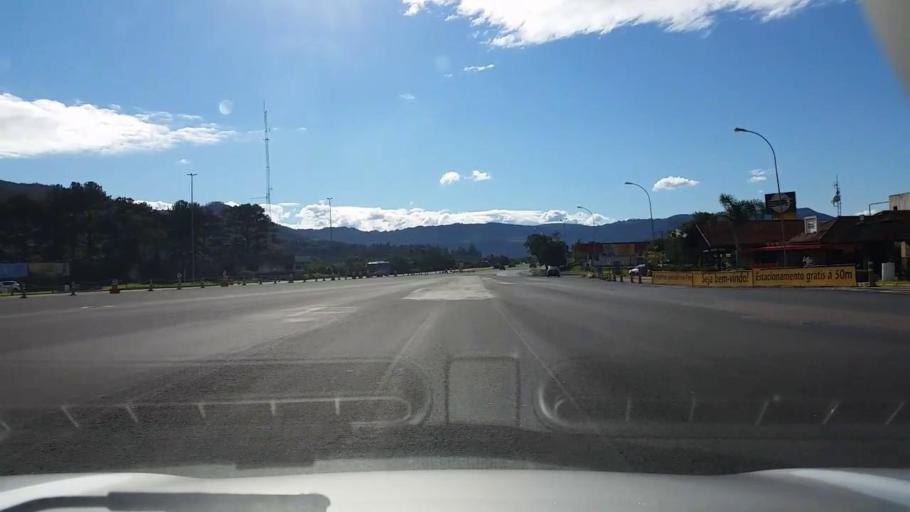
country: BR
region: Rio Grande do Sul
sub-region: Osorio
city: Osorio
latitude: -29.8851
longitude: -50.4461
